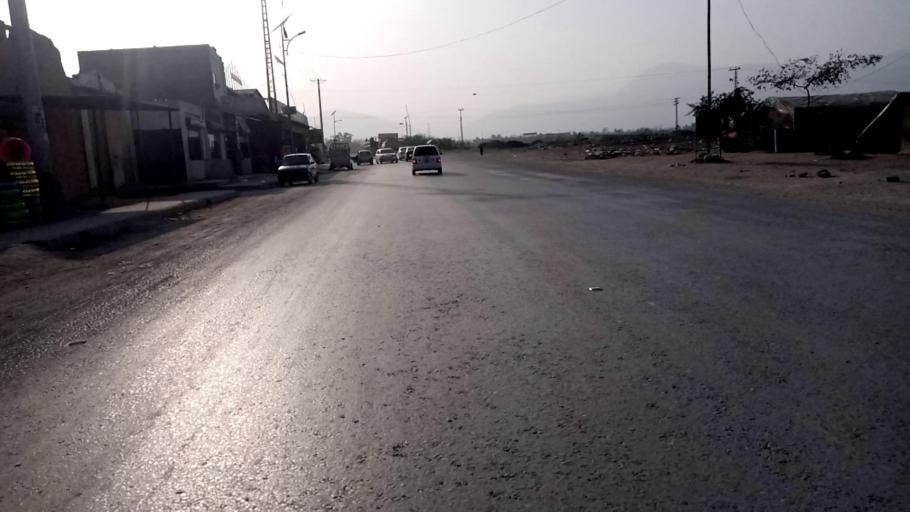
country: PK
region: Khyber Pakhtunkhwa
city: Peshawar
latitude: 33.9993
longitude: 71.4084
